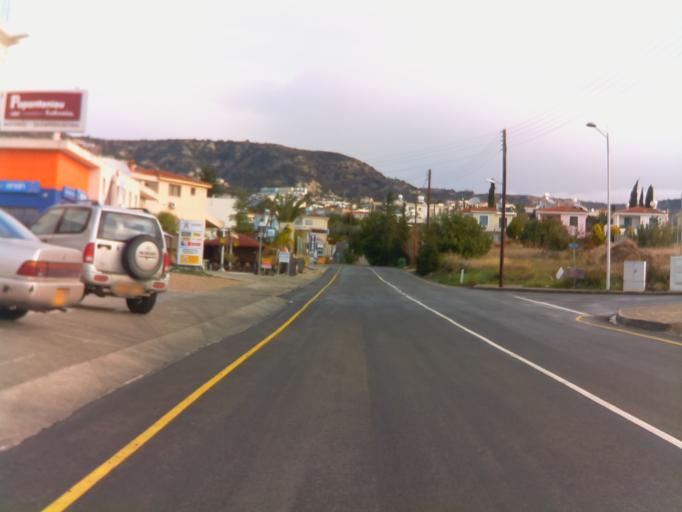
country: CY
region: Pafos
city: Pegeia
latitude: 34.8752
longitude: 32.3794
